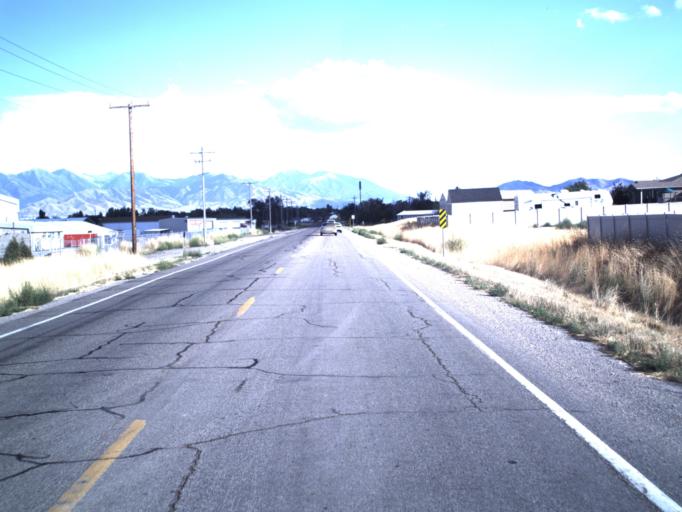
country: US
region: Utah
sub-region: Tooele County
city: Grantsville
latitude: 40.6054
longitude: -112.4878
